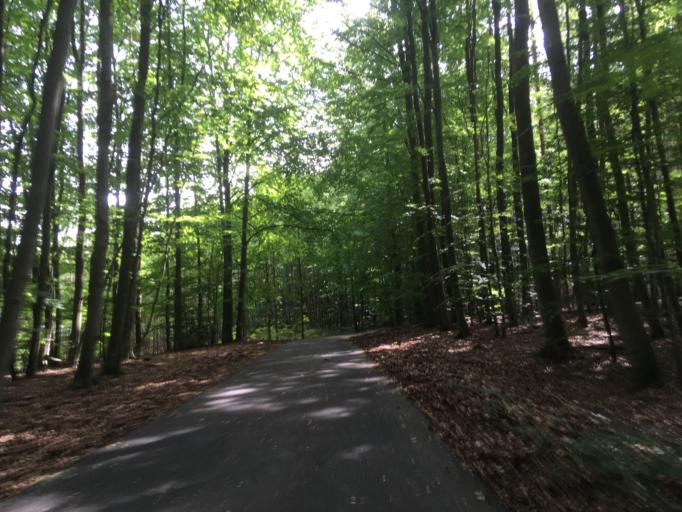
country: DE
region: Brandenburg
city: Wandlitz
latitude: 52.7364
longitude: 13.5003
